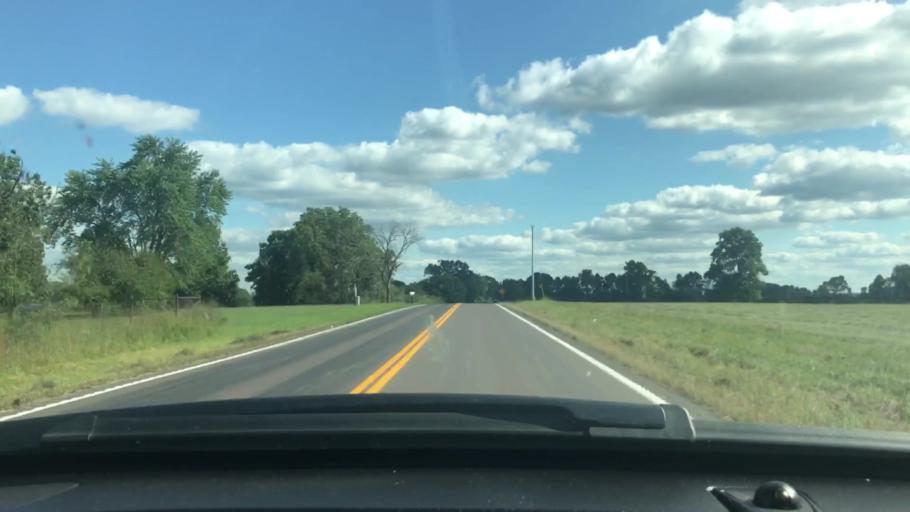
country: US
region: Missouri
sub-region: Wright County
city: Mountain Grove
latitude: 37.1797
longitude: -92.2687
